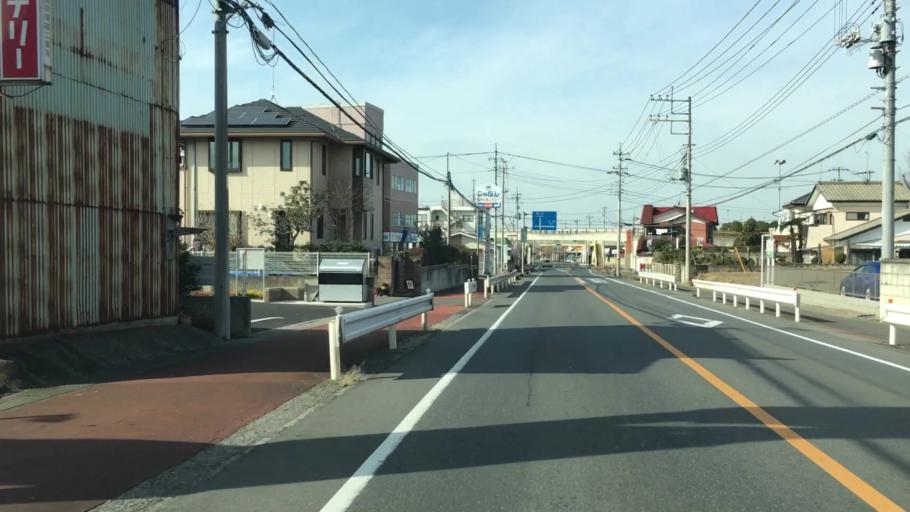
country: JP
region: Saitama
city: Menuma
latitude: 36.2437
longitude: 139.3936
